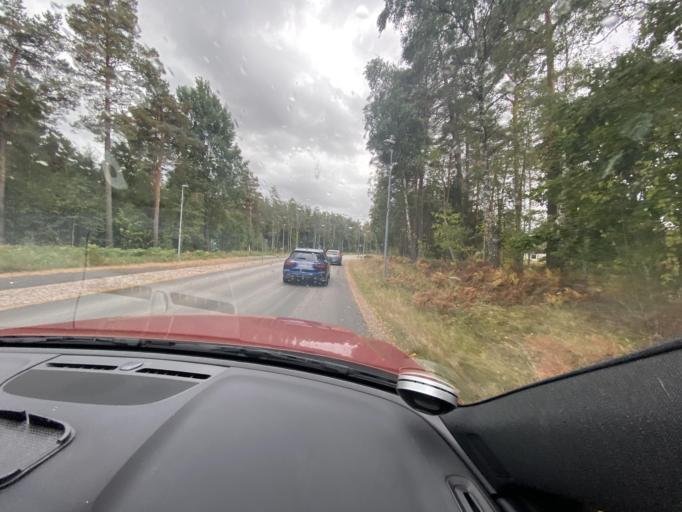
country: SE
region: Kronoberg
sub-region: Markaryds Kommun
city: Markaryd
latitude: 56.4564
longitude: 13.6187
